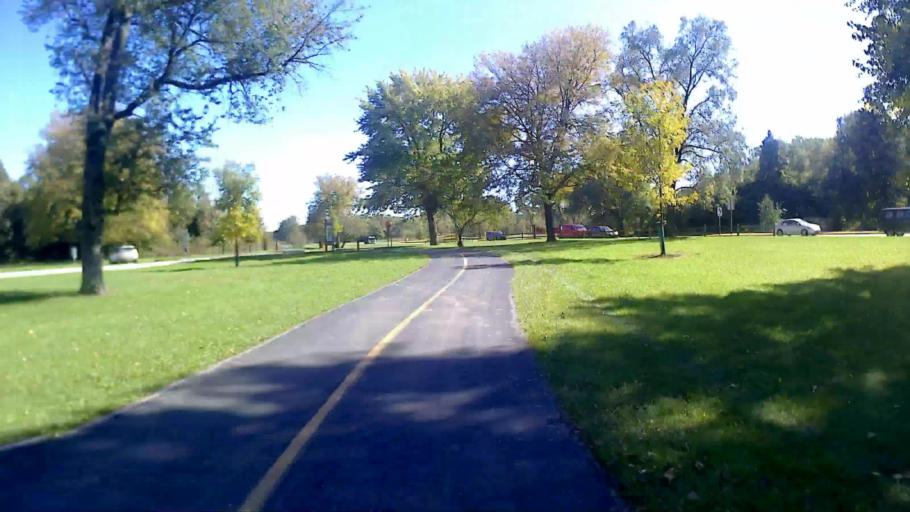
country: US
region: Illinois
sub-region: Cook County
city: Rolling Meadows
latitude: 42.0330
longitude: -88.0146
